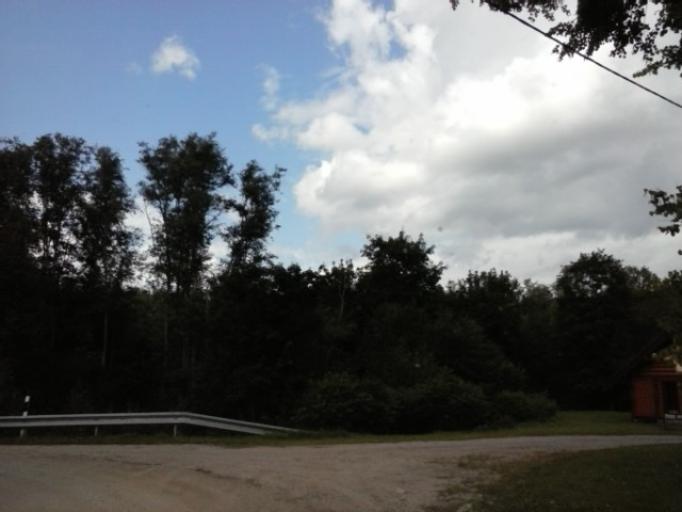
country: EE
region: Vorumaa
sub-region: Voru linn
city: Voru
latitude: 57.7679
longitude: 27.1572
